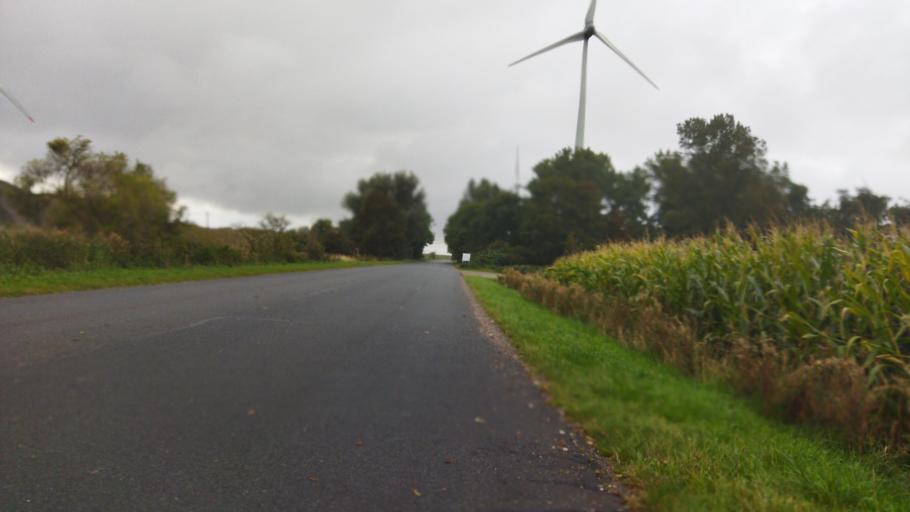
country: DE
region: Lower Saxony
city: Emden
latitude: 53.3417
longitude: 7.1365
